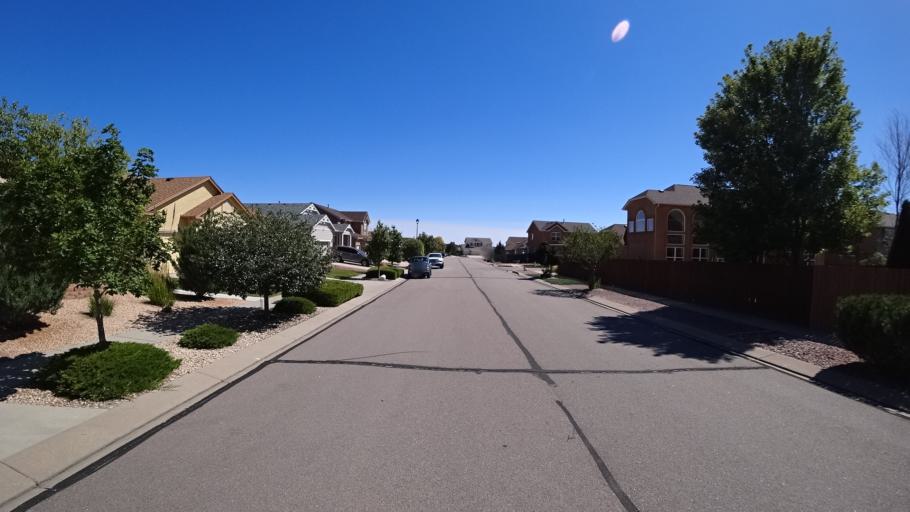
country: US
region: Colorado
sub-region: El Paso County
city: Security-Widefield
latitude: 38.7858
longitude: -104.7266
